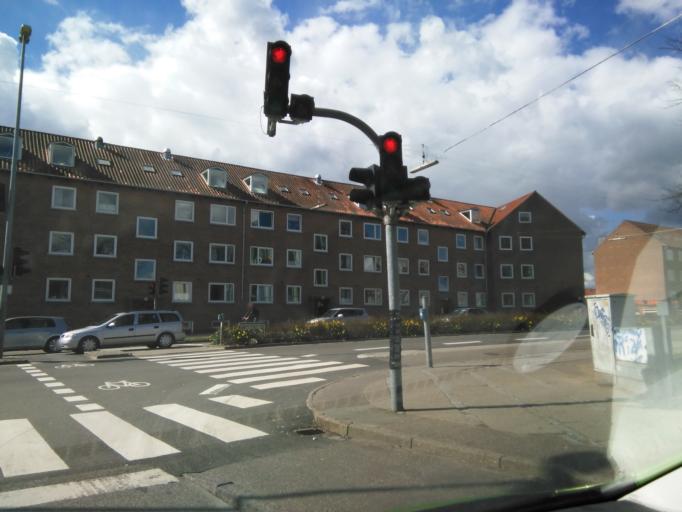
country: DK
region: Central Jutland
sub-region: Arhus Kommune
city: Arhus
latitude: 56.1690
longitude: 10.1891
